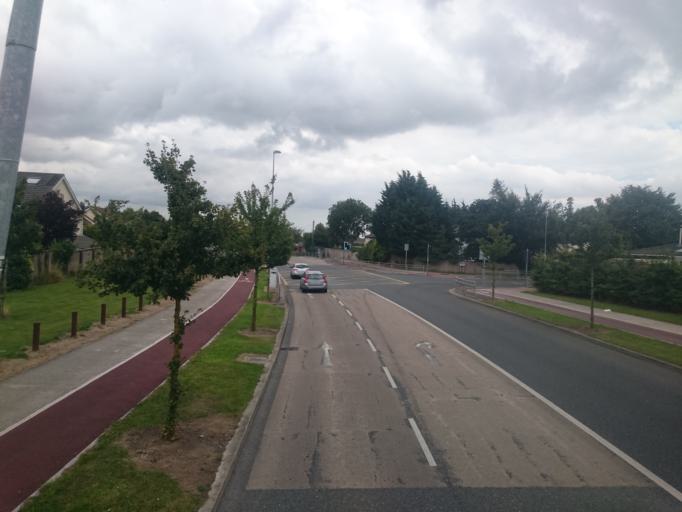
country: IE
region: Leinster
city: Firhouse
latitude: 53.2777
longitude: -6.3478
